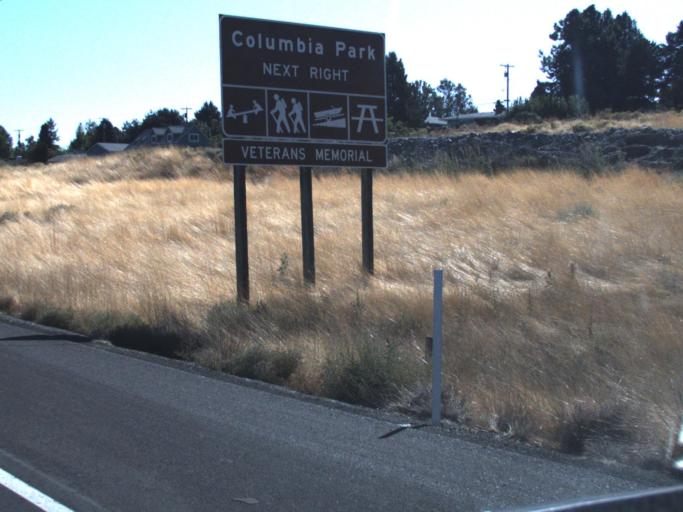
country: US
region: Washington
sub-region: Franklin County
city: West Pasco
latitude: 46.2304
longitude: -119.2022
